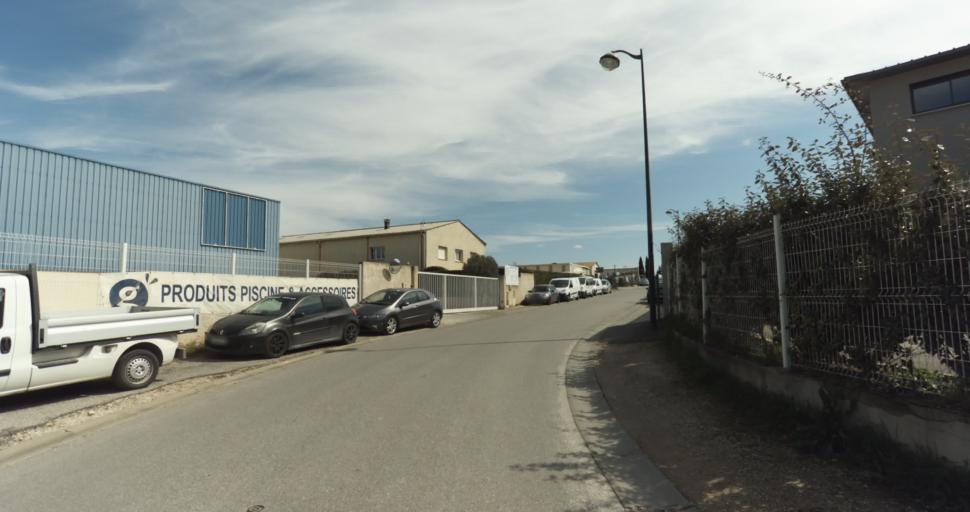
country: FR
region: Provence-Alpes-Cote d'Azur
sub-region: Departement des Bouches-du-Rhone
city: Saint-Cannat
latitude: 43.6140
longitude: 5.3193
